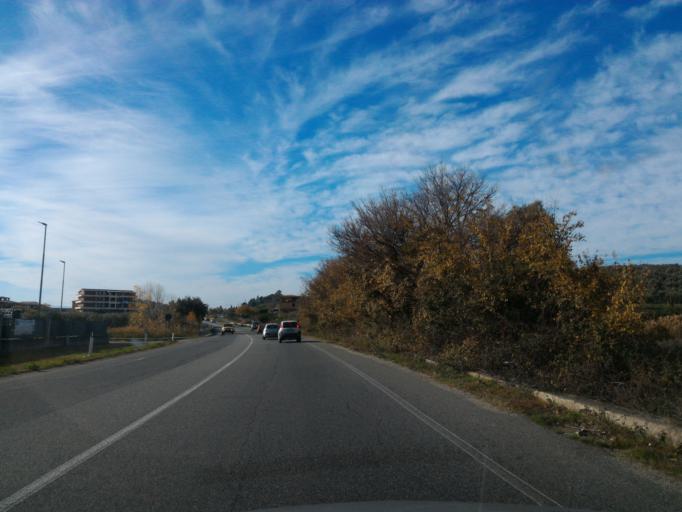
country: IT
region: Calabria
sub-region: Provincia di Catanzaro
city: Sellia Marina
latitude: 38.8933
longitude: 16.7238
